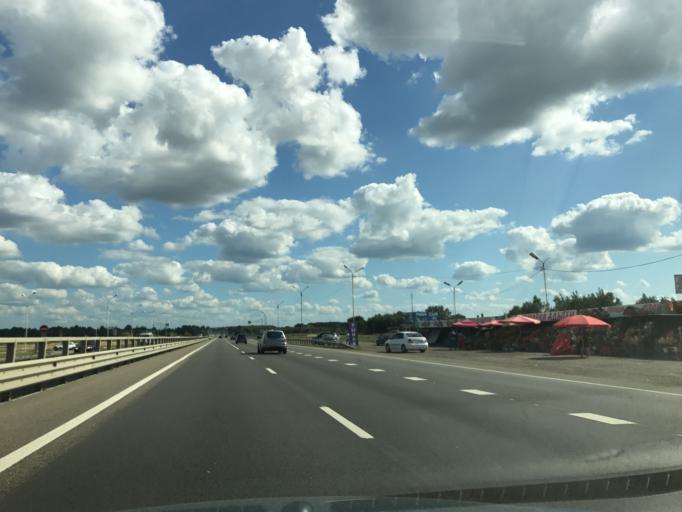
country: RU
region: Adygeya
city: Adygeysk
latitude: 44.8382
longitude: 39.2137
